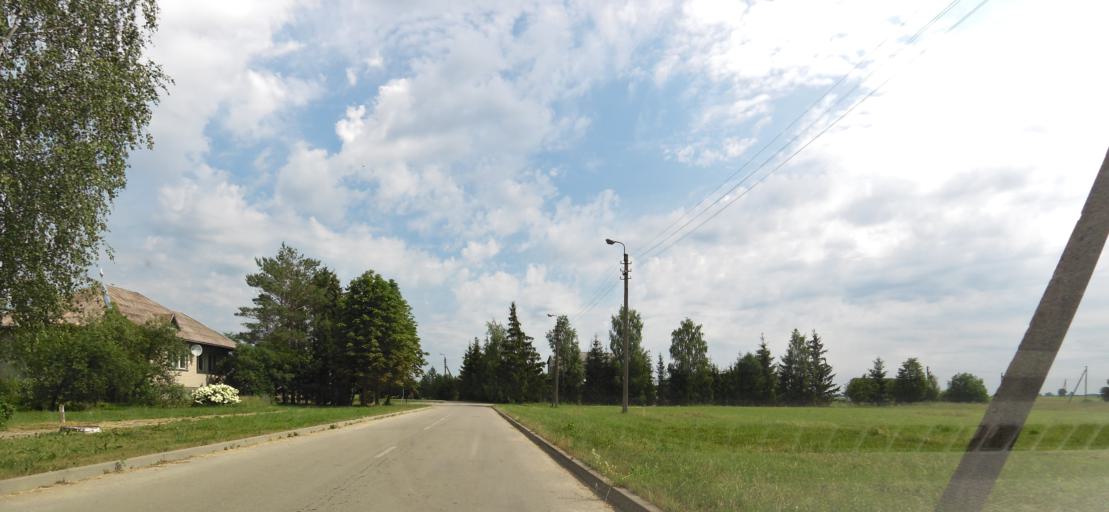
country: LT
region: Panevezys
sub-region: Birzai
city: Birzai
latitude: 56.2652
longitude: 24.6163
